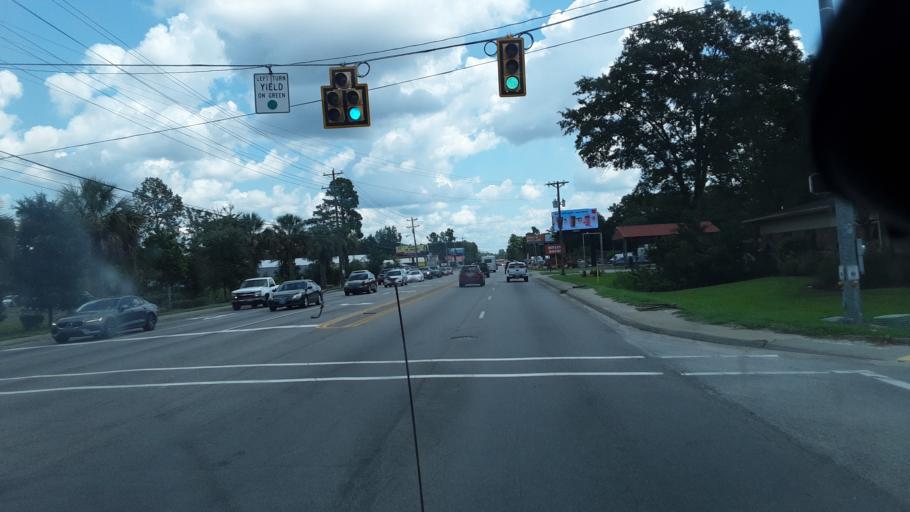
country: US
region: South Carolina
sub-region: Berkeley County
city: Sangaree
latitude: 33.0440
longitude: -80.1203
